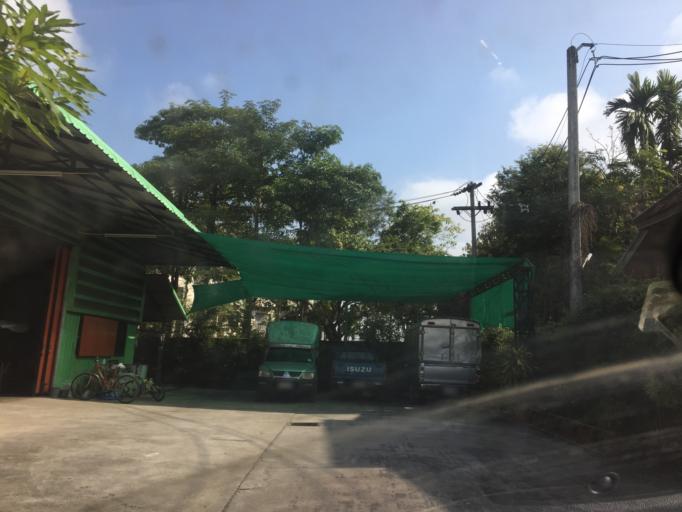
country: TH
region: Chiang Mai
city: Saraphi
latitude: 18.6488
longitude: 99.0501
